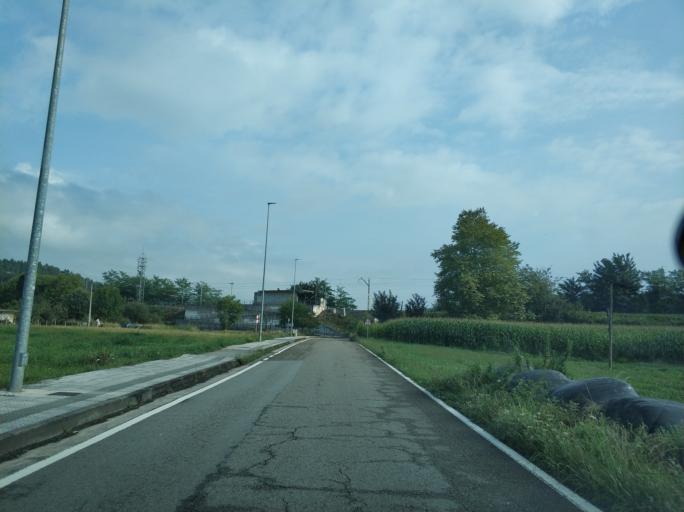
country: ES
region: Cantabria
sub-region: Provincia de Cantabria
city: Polanco
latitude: 43.3596
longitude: -3.9647
